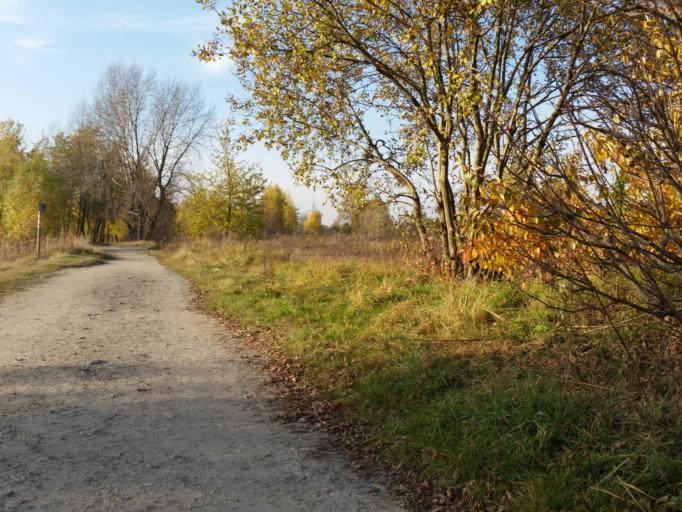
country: PL
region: Silesian Voivodeship
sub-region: Sosnowiec
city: Sosnowiec
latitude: 50.2676
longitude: 19.1191
